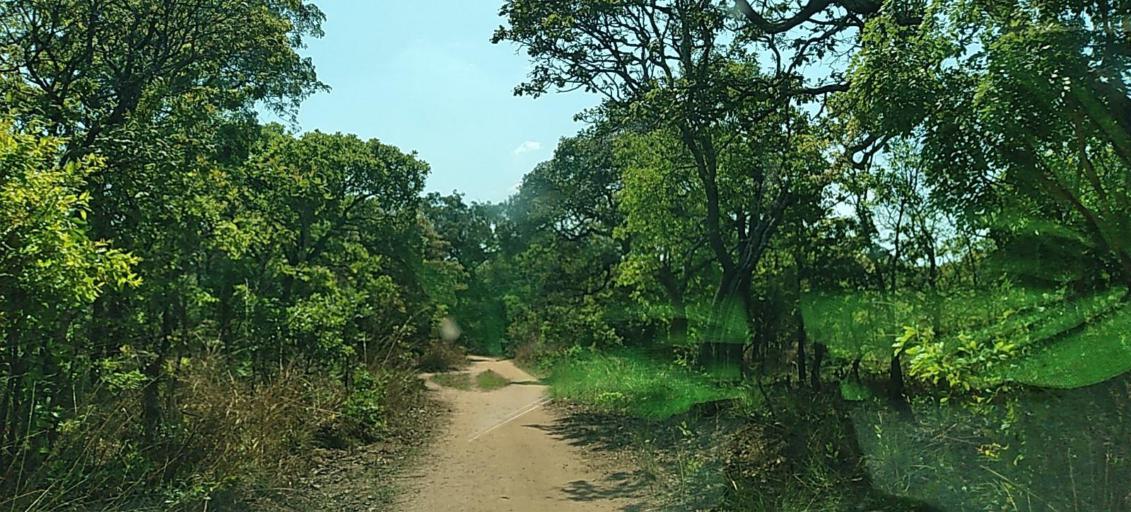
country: CD
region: Katanga
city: Kolwezi
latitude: -11.2764
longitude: 25.1169
